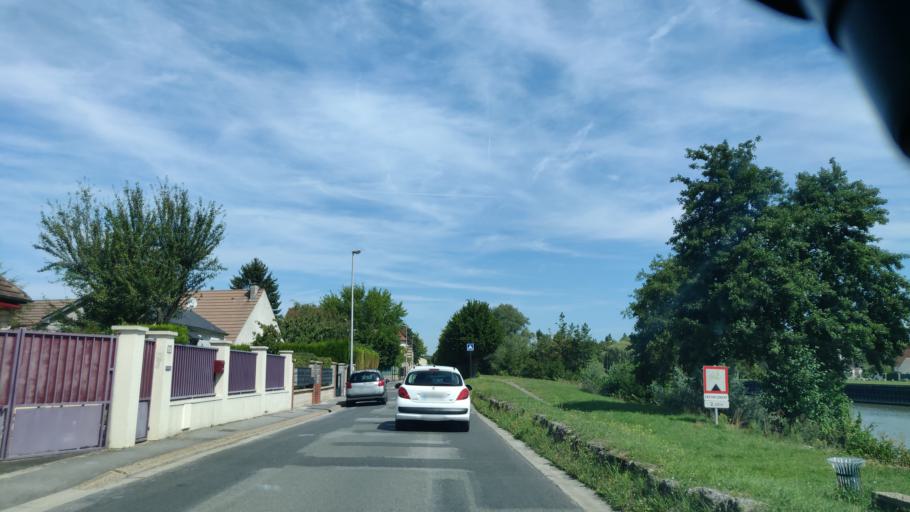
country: FR
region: Picardie
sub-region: Departement de l'Oise
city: Pont-Sainte-Maxence
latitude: 49.3051
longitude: 2.6107
